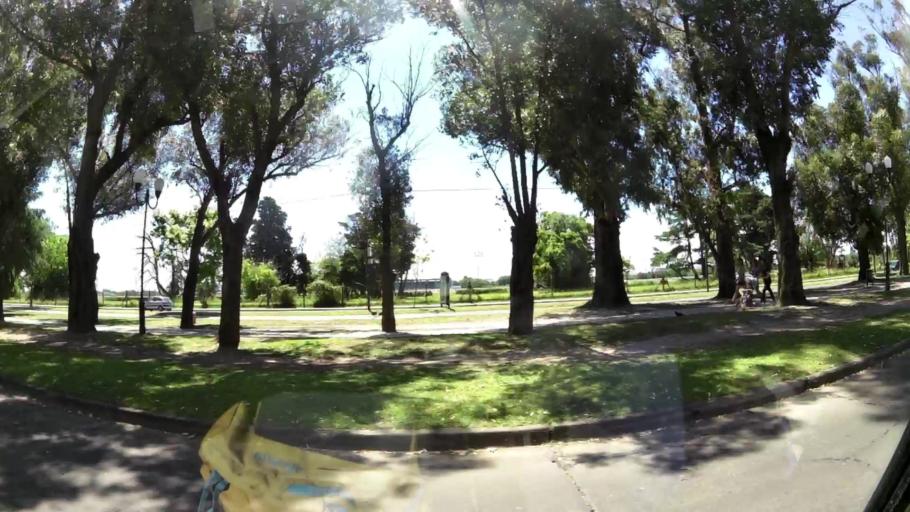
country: AR
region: Buenos Aires
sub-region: Partido de San Isidro
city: San Isidro
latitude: -34.4846
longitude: -58.5148
